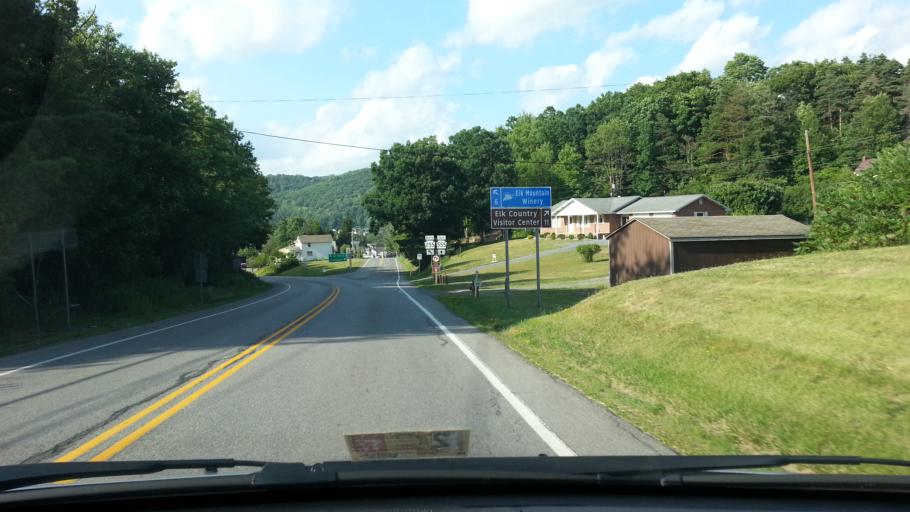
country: US
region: Pennsylvania
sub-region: Elk County
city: Saint Marys
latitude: 41.2694
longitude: -78.4963
